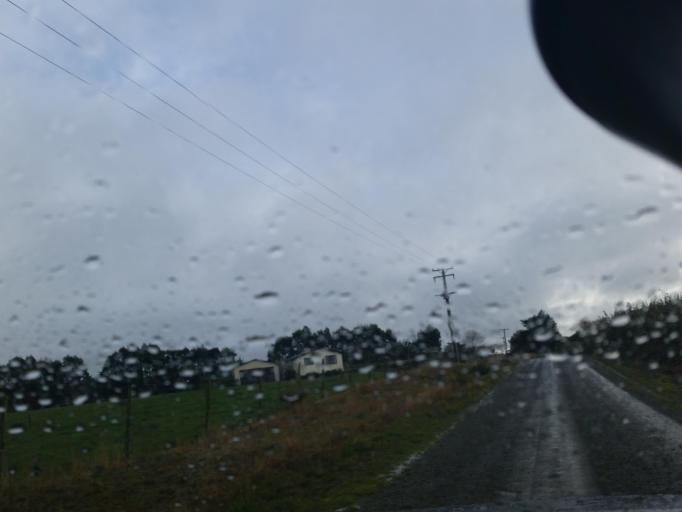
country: NZ
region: Southland
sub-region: Southland District
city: Winton
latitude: -46.2076
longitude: 168.2198
